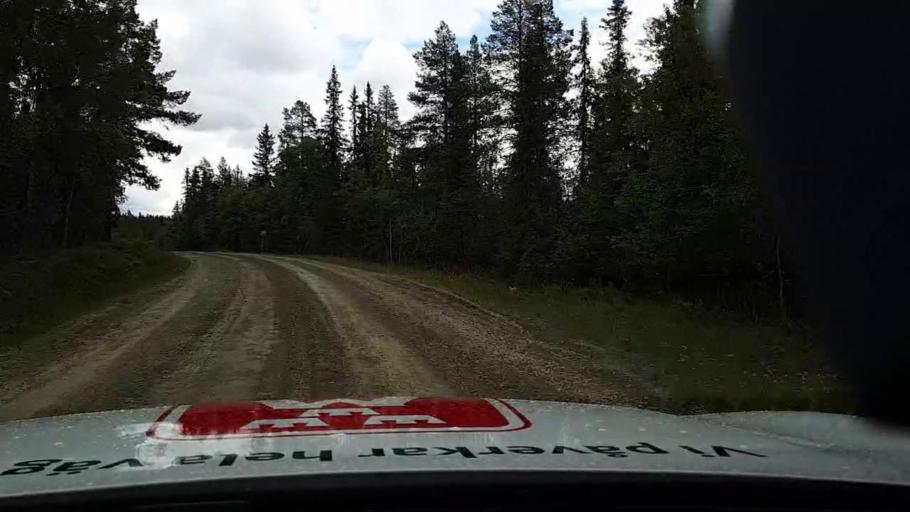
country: SE
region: Jaemtland
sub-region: Are Kommun
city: Jarpen
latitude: 62.6070
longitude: 13.2116
